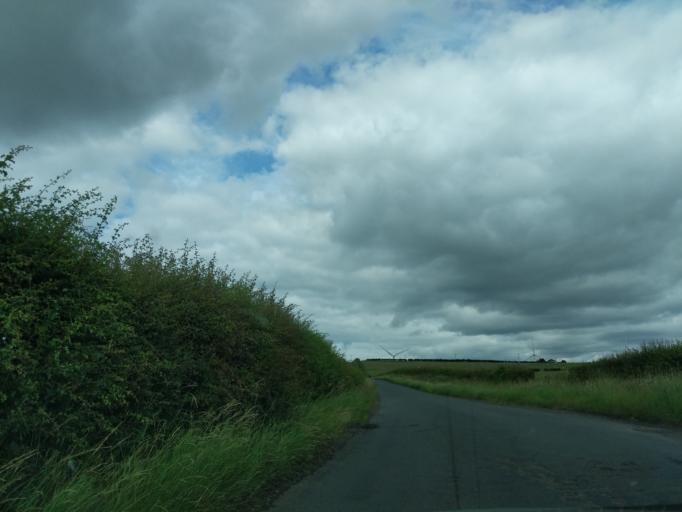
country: GB
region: Scotland
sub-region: South Lanarkshire
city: Larkhall
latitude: 55.7014
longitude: -3.9641
